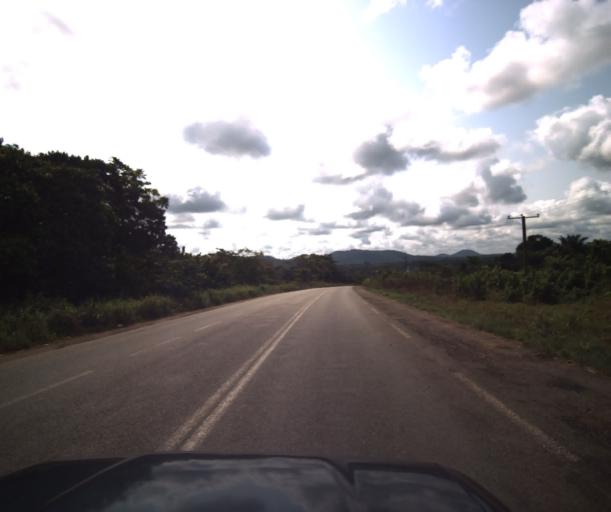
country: CM
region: Littoral
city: Edea
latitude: 3.7829
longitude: 10.1557
